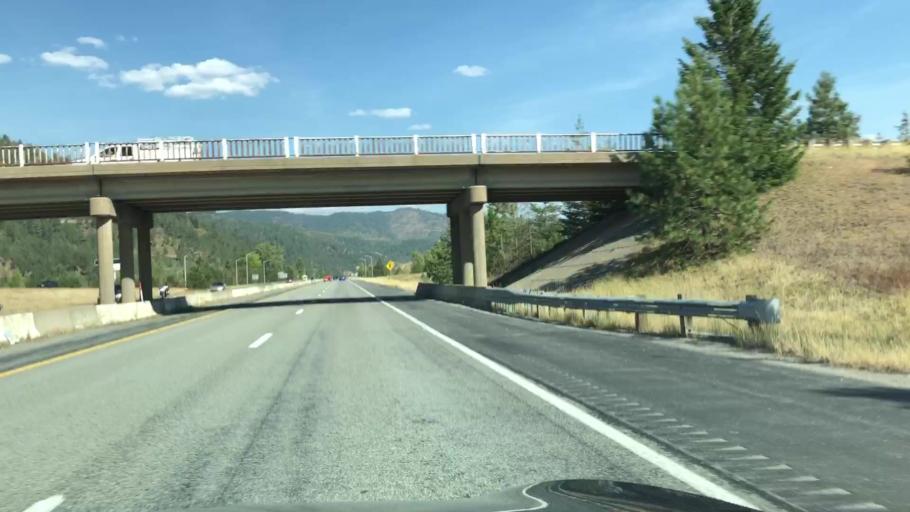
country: US
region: Idaho
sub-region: Shoshone County
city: Kellogg
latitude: 47.5465
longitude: -116.1757
